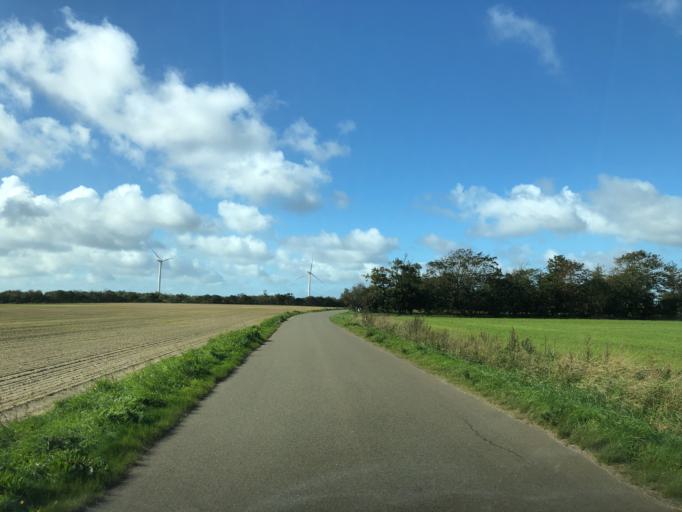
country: DK
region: Central Jutland
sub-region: Holstebro Kommune
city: Ulfborg
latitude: 56.2904
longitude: 8.3255
